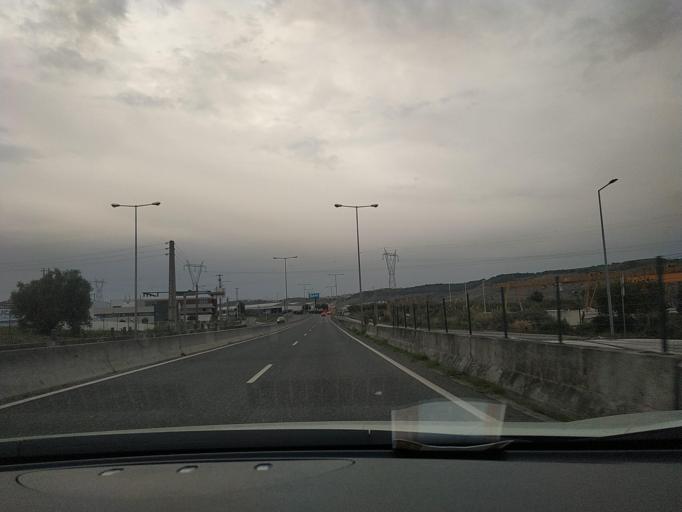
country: PT
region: Lisbon
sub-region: Loures
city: Santo Antao do Tojal
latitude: 38.8609
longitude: -9.1184
